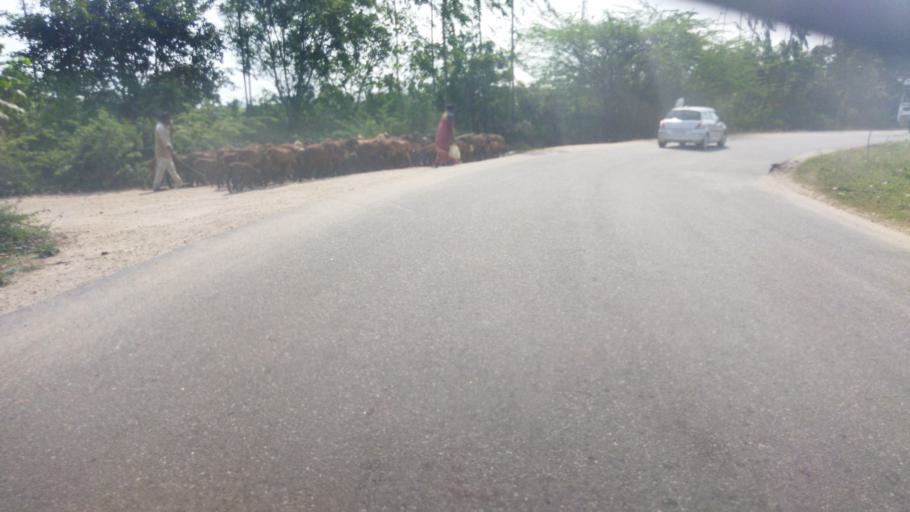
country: IN
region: Telangana
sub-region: Nalgonda
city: Nalgonda
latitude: 17.1543
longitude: 79.3113
